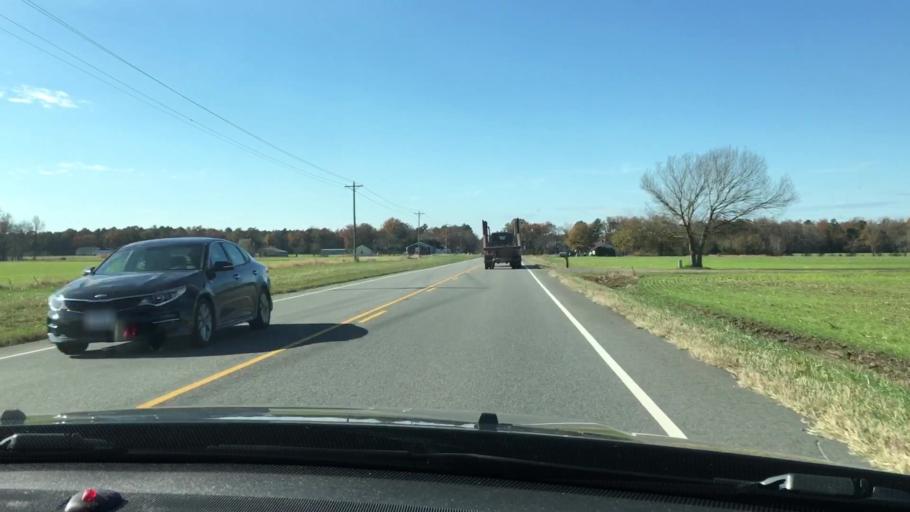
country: US
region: Virginia
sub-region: Hanover County
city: Hanover
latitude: 37.8123
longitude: -77.2947
